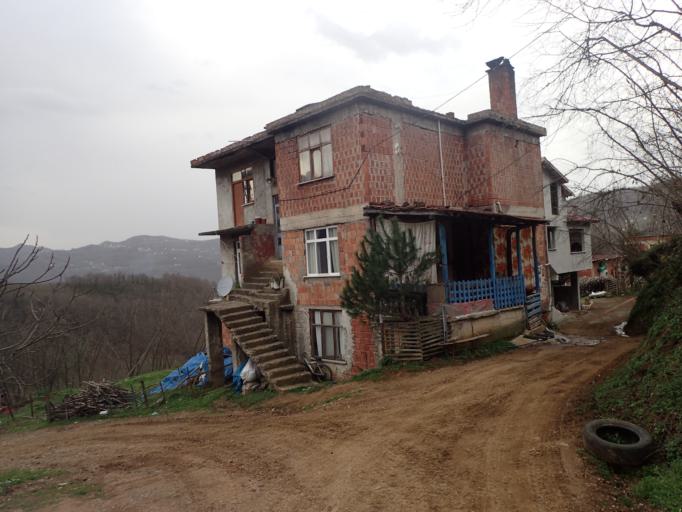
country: TR
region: Ordu
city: Camas
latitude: 40.8920
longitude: 37.4951
